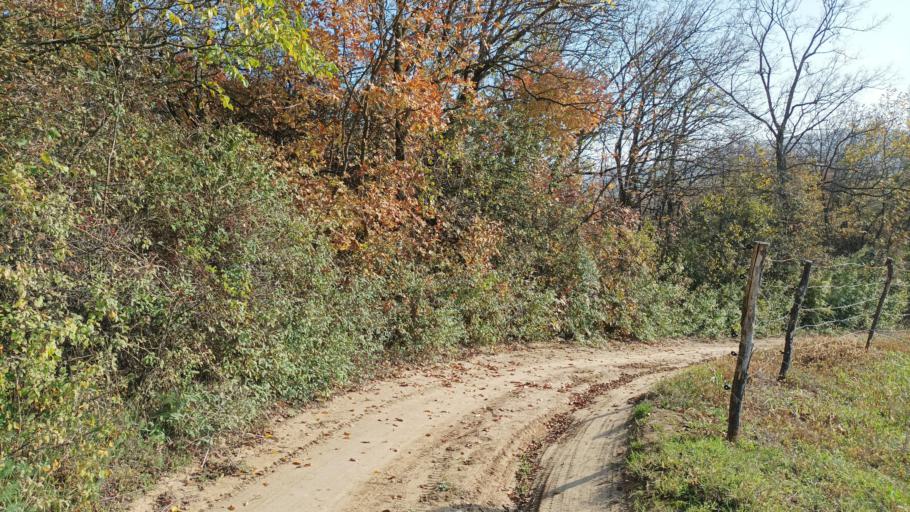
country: HU
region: Tolna
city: Szentgalpuszta
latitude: 46.3434
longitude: 18.6024
